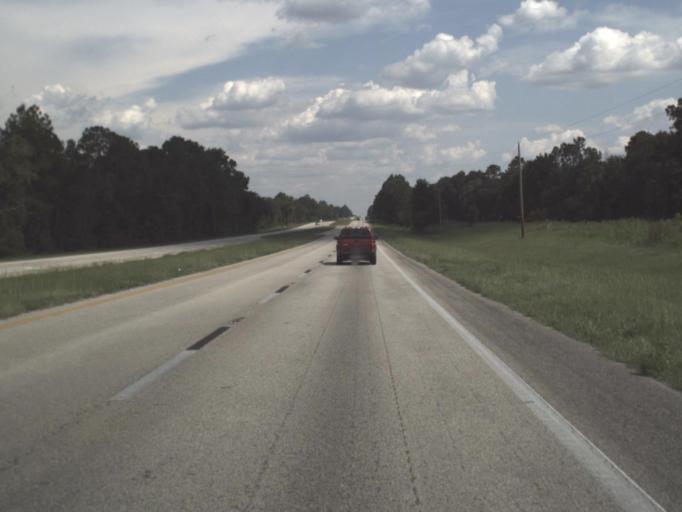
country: US
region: Florida
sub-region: Alachua County
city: Hawthorne
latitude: 29.6864
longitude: -82.1267
